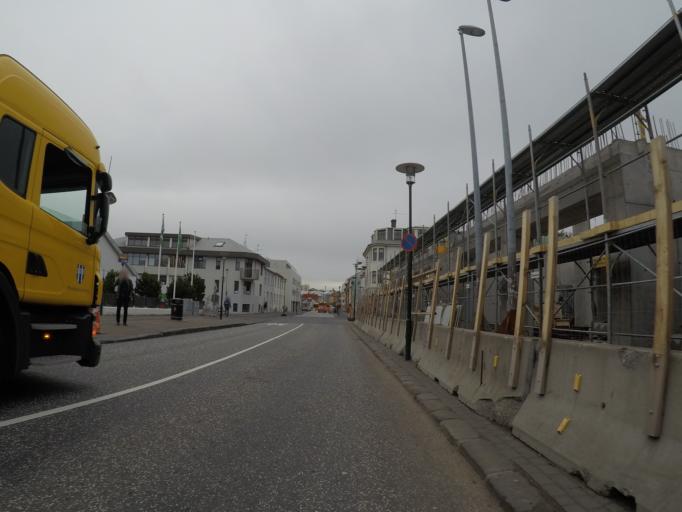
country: IS
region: Capital Region
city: Reykjavik
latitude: 64.1445
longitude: -21.9192
